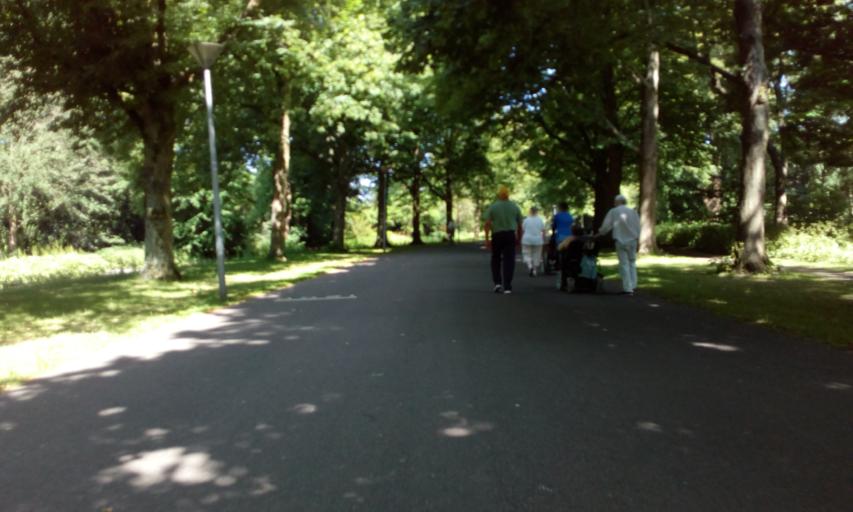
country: NL
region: South Holland
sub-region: Gemeente Den Haag
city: The Hague
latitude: 52.0555
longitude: 4.2799
